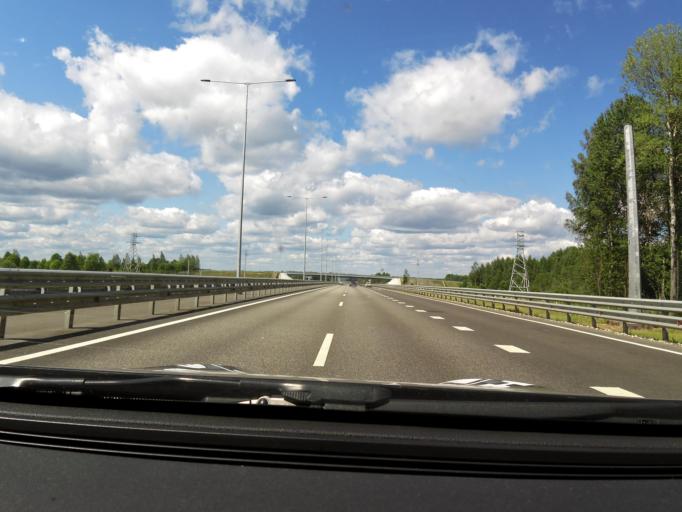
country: RU
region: Tverskaya
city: Vydropuzhsk
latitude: 57.3727
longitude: 34.6190
